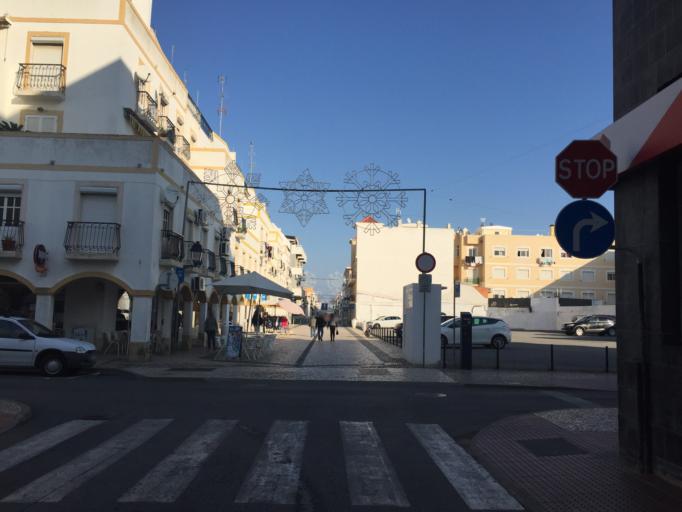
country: PT
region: Faro
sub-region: Vila Real de Santo Antonio
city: Vila Real de Santo Antonio
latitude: 37.1936
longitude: -7.4186
